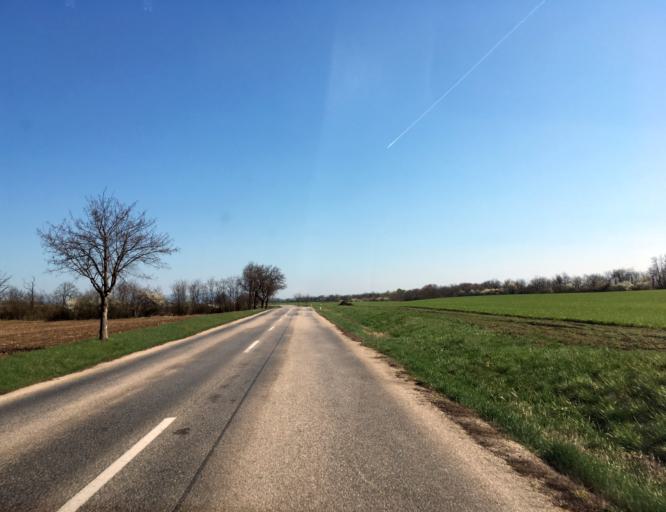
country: HU
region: Komarom-Esztergom
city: Nyergesujfalu
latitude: 47.8257
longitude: 18.5598
